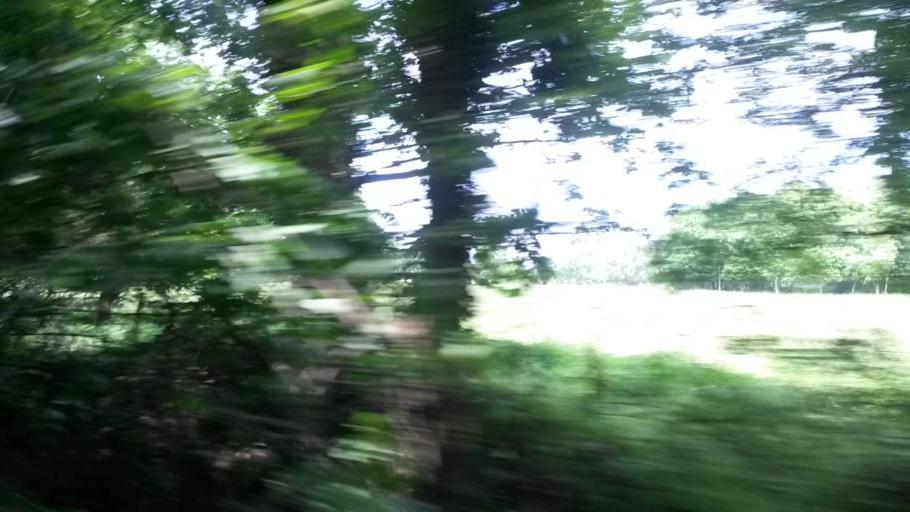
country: IE
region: Leinster
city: Donabate
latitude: 53.4908
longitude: -6.1741
